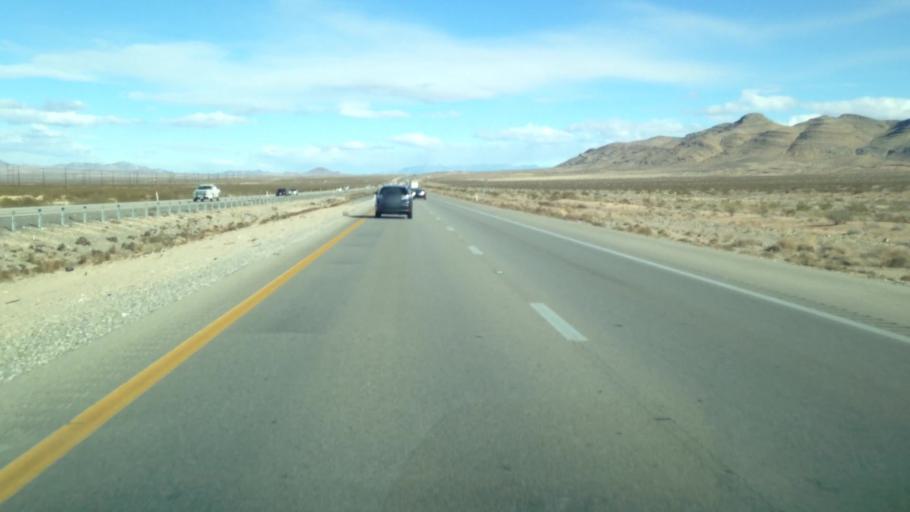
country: US
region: Nevada
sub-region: Clark County
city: Nellis Air Force Base
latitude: 36.4183
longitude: -114.8667
